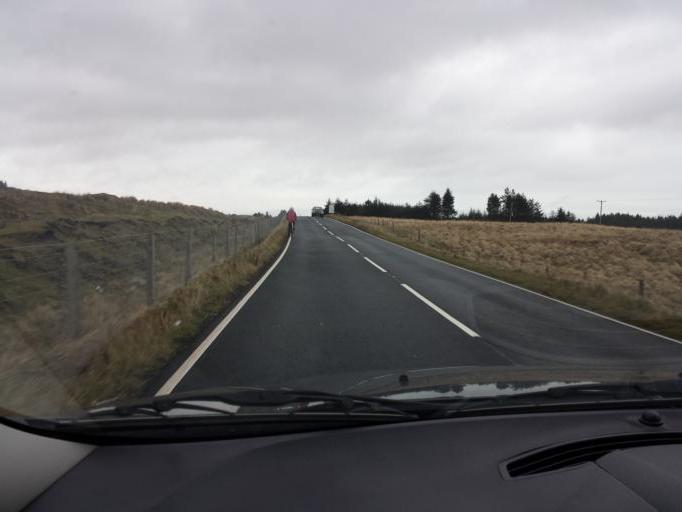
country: GB
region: Northern Ireland
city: Glenariff
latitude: 55.0081
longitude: -6.1515
